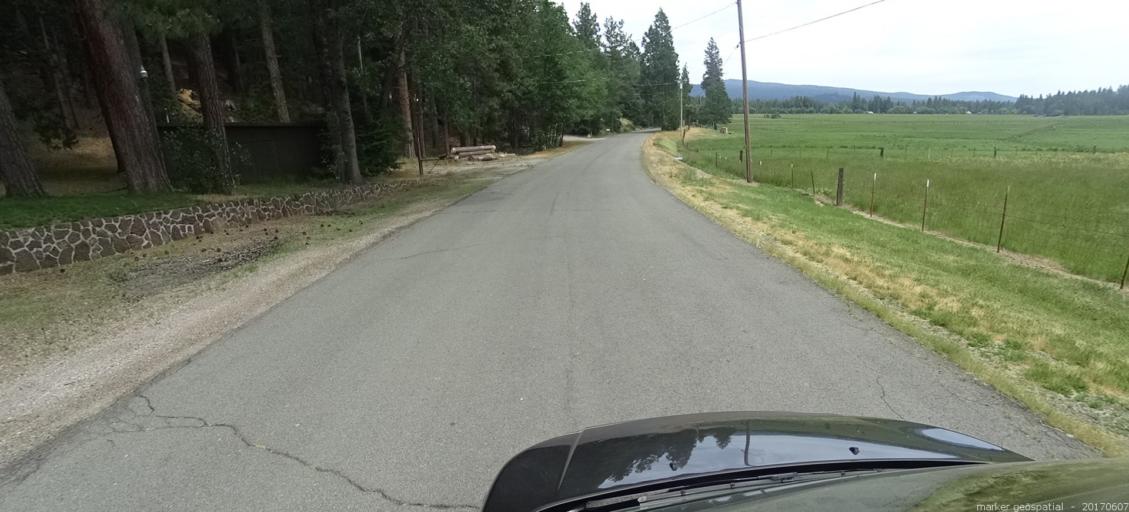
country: US
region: California
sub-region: Siskiyou County
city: Mount Shasta
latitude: 41.3253
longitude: -122.3583
